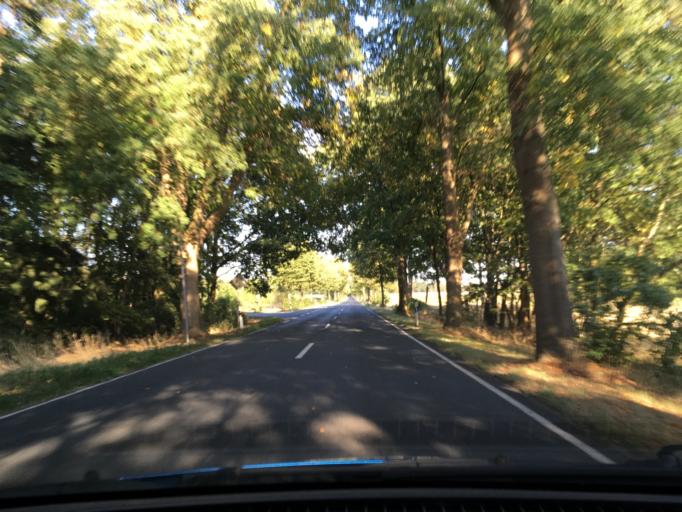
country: DE
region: Lower Saxony
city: Burgdorf
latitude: 52.4777
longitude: 9.9285
